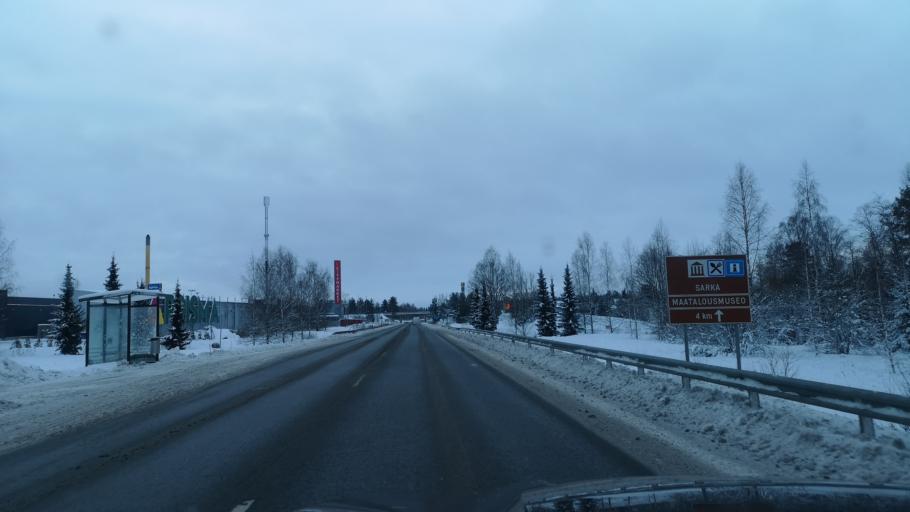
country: FI
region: Varsinais-Suomi
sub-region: Loimaa
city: Loimaa
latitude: 60.8583
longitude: 23.0441
